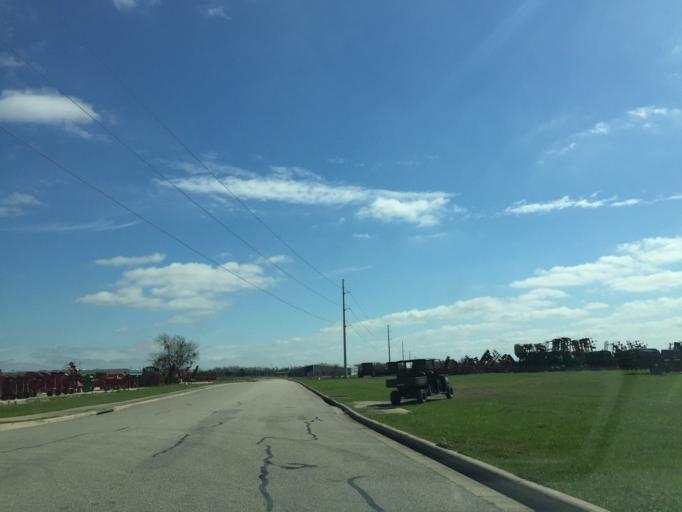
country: US
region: Texas
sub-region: Williamson County
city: Taylor
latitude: 30.5617
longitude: -97.4303
